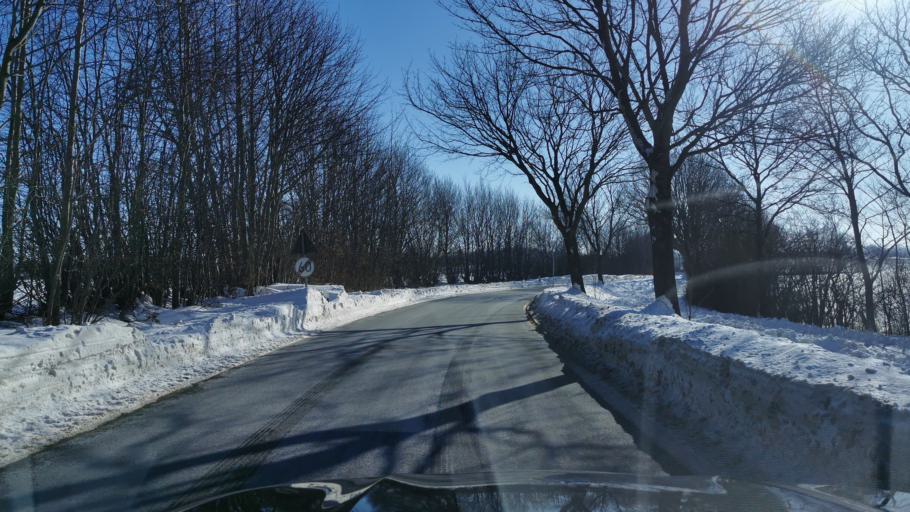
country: DE
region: Schleswig-Holstein
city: Sorup
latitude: 54.7437
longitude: 9.6440
